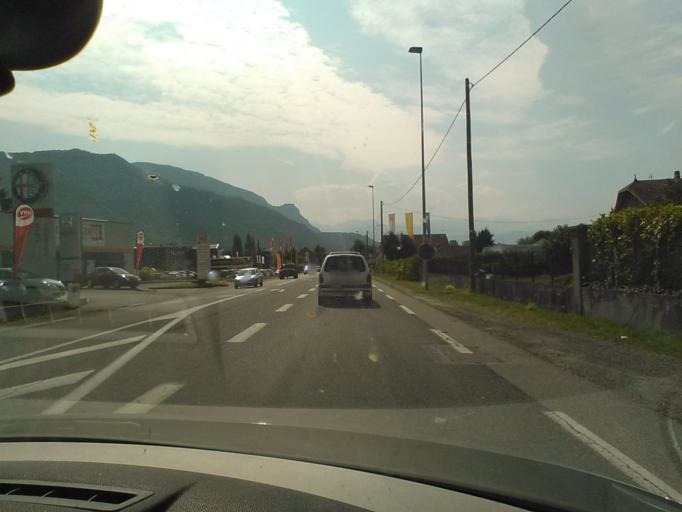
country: FR
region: Rhone-Alpes
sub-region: Departement de la Savoie
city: La Ravoire
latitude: 45.5635
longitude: 5.9688
